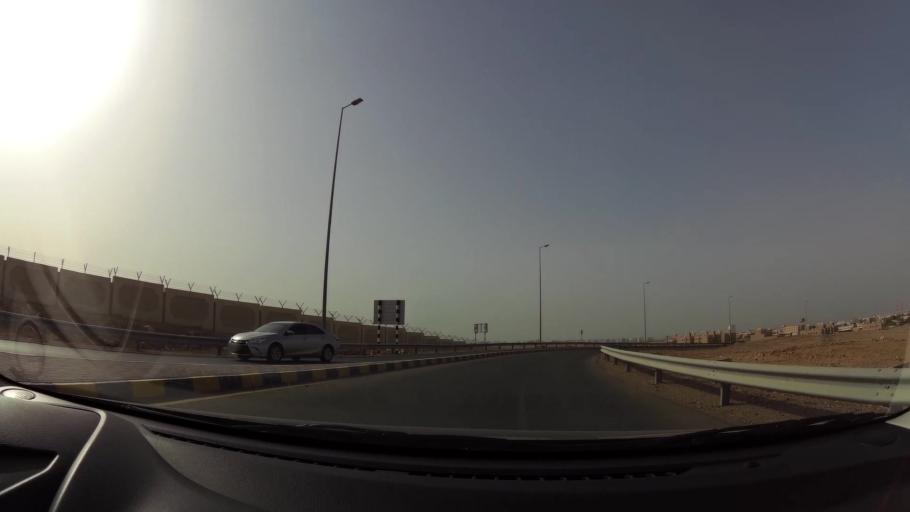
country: OM
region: Muhafazat Masqat
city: Bawshar
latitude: 23.5571
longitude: 58.3667
